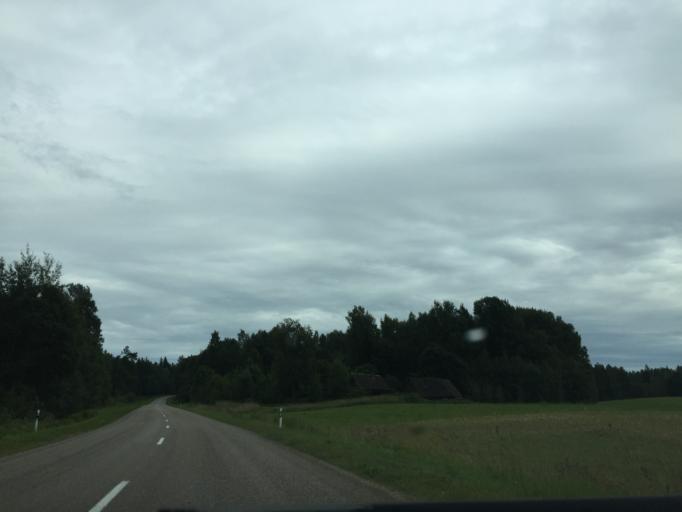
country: LV
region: Dagda
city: Dagda
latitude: 56.1866
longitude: 27.3611
